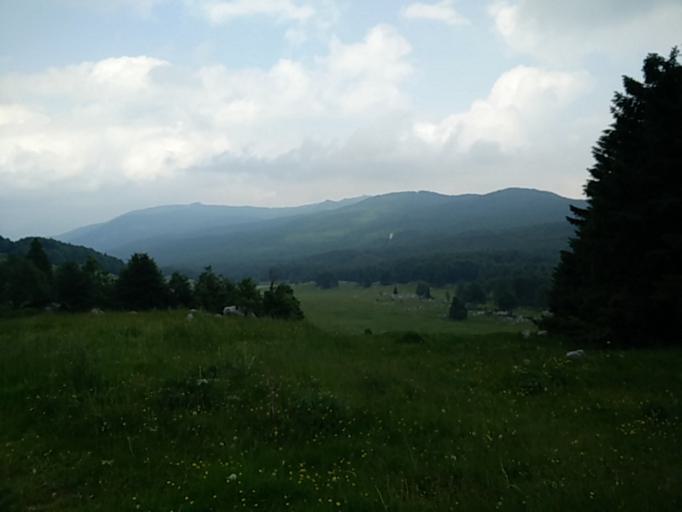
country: IT
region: Friuli Venezia Giulia
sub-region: Provincia di Pordenone
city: Budoia
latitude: 46.1160
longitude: 12.5166
